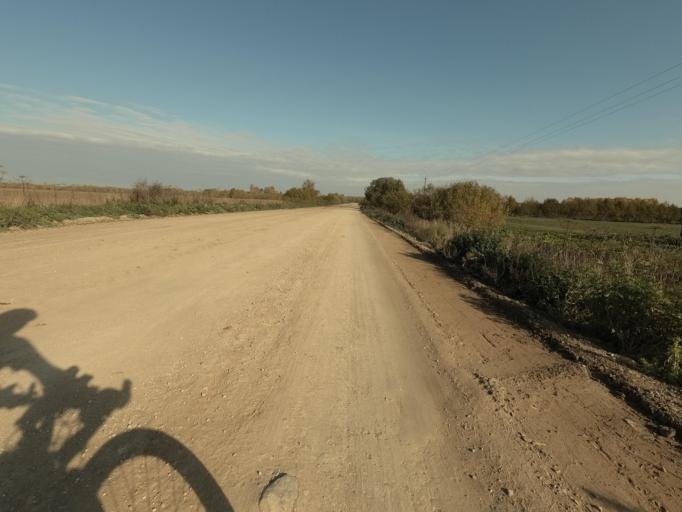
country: RU
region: Novgorod
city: Batetskiy
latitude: 58.8141
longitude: 30.6977
